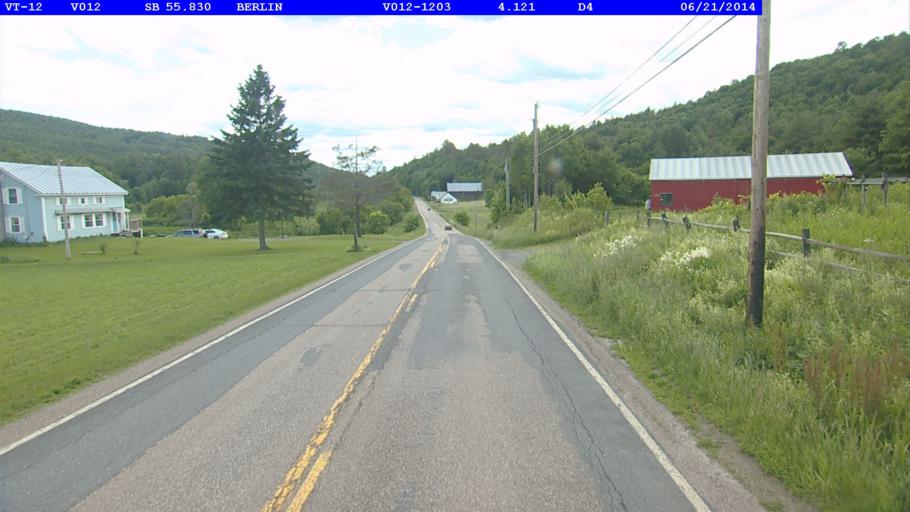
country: US
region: Vermont
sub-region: Washington County
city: Montpelier
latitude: 44.2256
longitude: -72.6213
